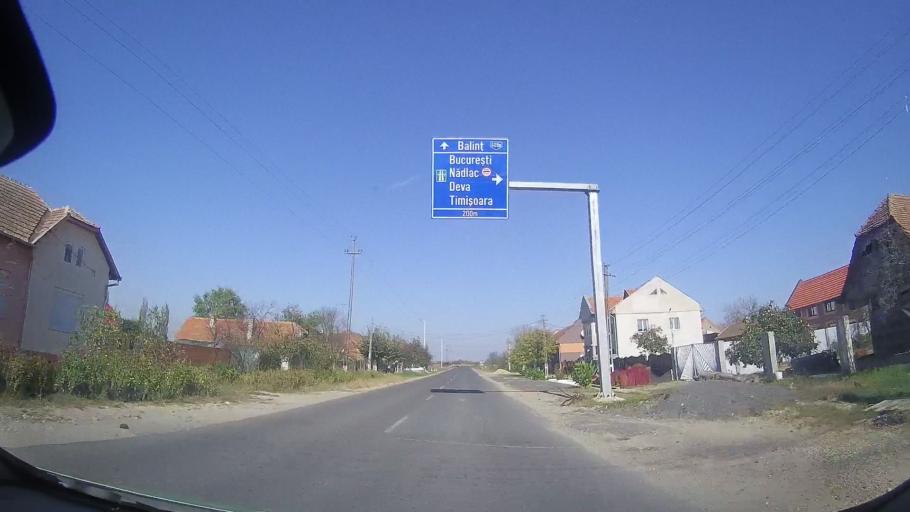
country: RO
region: Timis
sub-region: Comuna Balint
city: Balint
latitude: 45.7779
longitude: 21.8481
